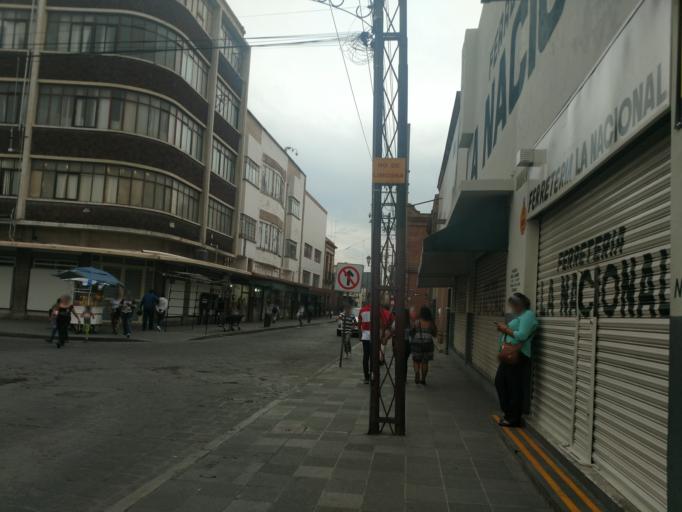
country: MX
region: San Luis Potosi
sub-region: San Luis Potosi
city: San Luis Potosi
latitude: 22.1547
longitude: -100.9759
